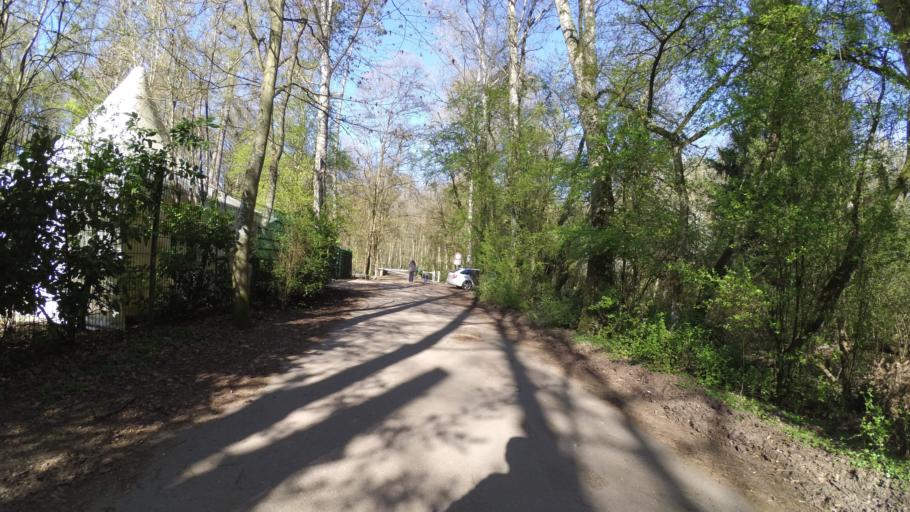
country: DE
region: Saarland
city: Volklingen
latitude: 49.2624
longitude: 6.8761
